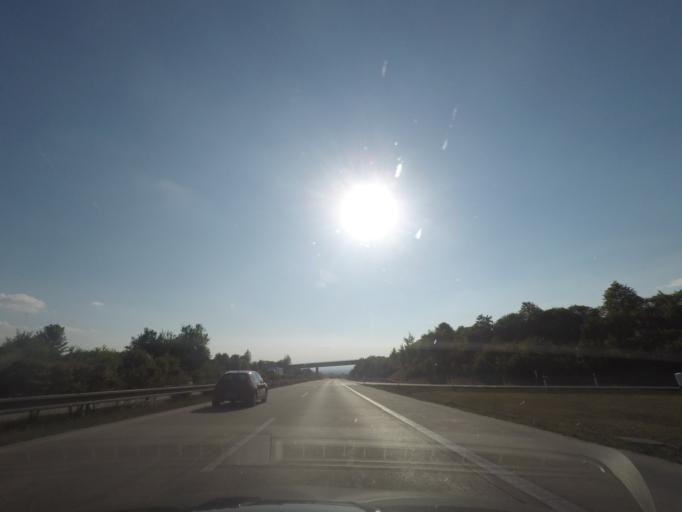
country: CZ
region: Olomoucky
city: Praslavice
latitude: 49.5774
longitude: 17.3814
